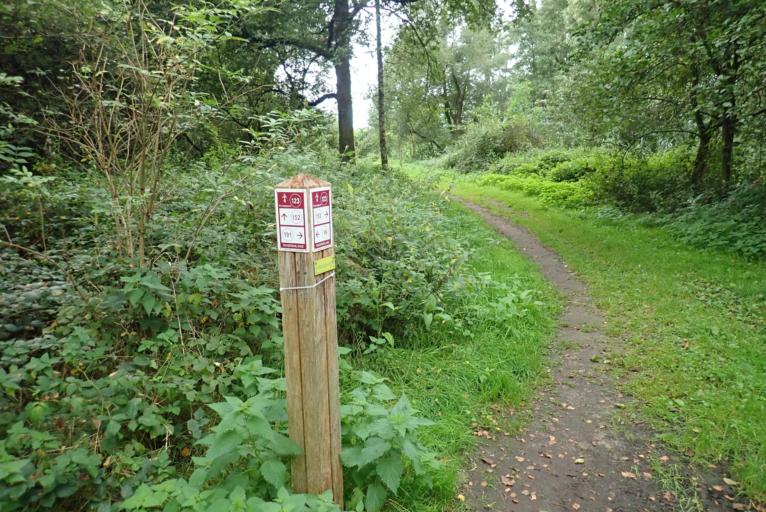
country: BE
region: Flanders
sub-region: Provincie Antwerpen
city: Boom
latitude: 51.0730
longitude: 4.3824
